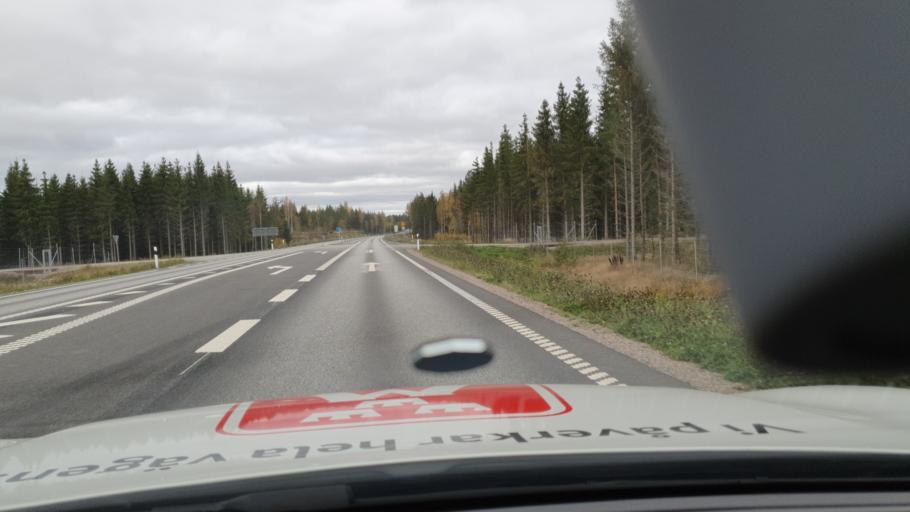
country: SE
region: OErebro
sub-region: Hallsbergs Kommun
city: Palsboda
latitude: 59.0559
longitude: 15.3249
